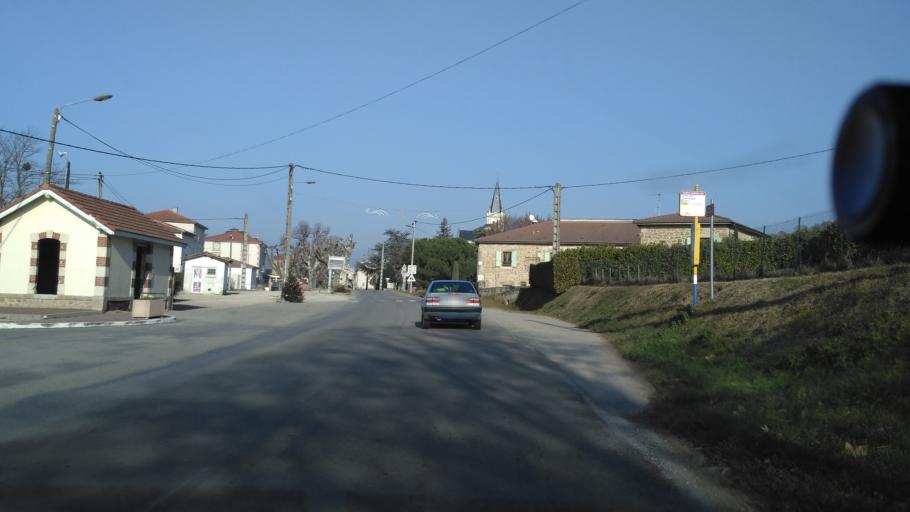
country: FR
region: Rhone-Alpes
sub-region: Departement de la Drome
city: Clerieux
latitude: 45.0737
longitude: 4.9587
